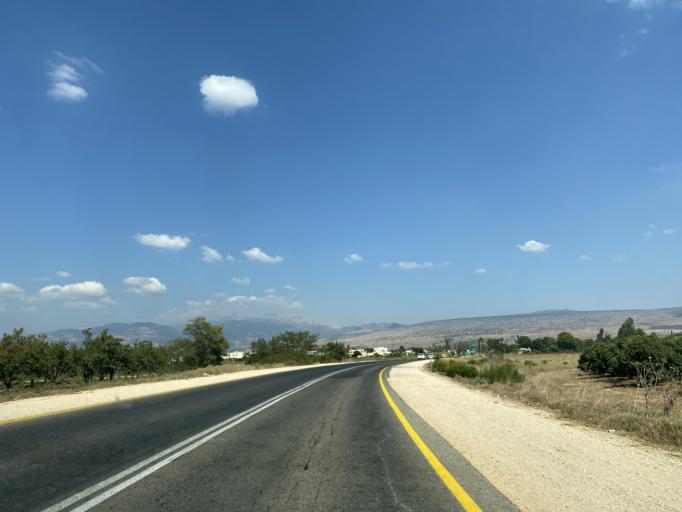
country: IL
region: Northern District
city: Qiryat Shemona
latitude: 33.1721
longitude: 35.6002
